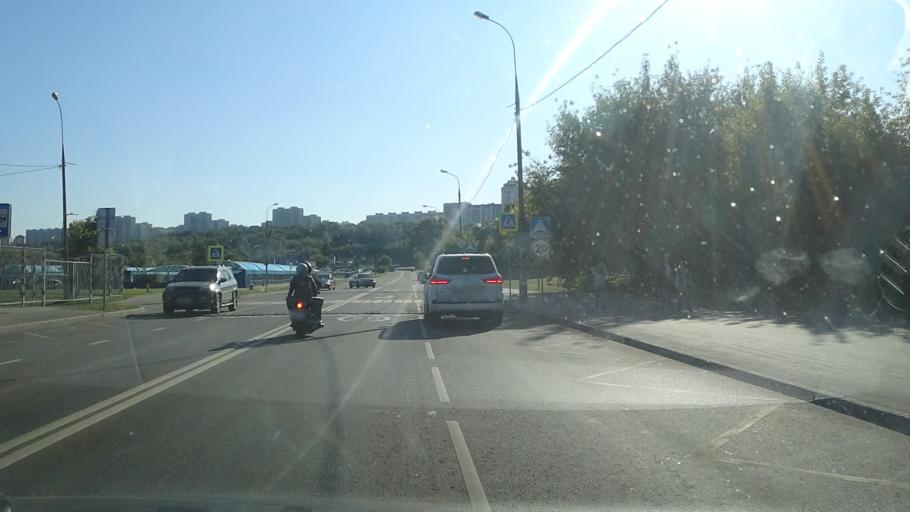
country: RU
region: Moskovskaya
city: Bol'shaya Setun'
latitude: 55.7545
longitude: 37.4328
